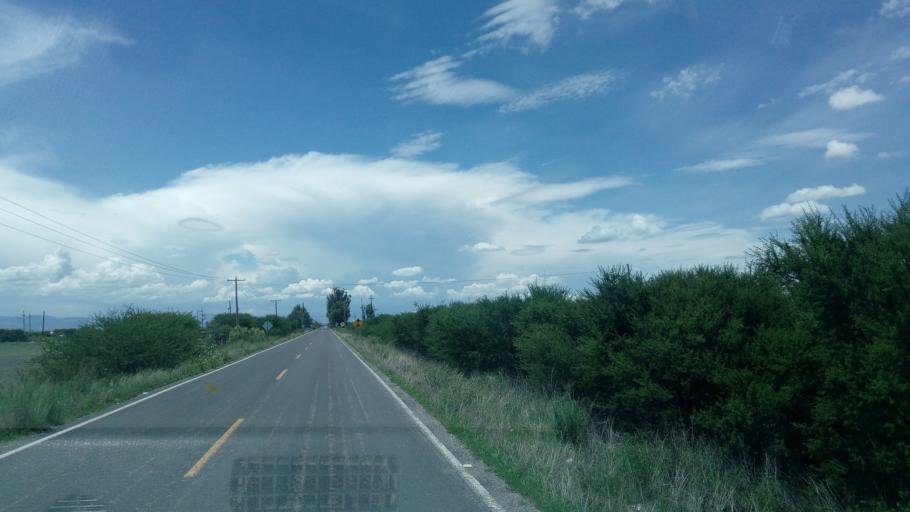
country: MX
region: Durango
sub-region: Durango
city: Jose Refugio Salcido
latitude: 24.1583
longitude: -104.5187
